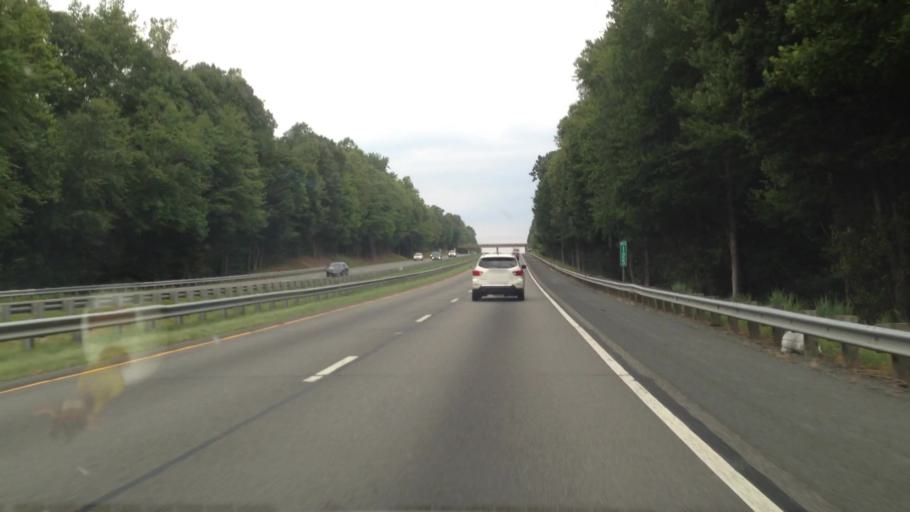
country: US
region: North Carolina
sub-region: Stokes County
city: King
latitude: 36.2800
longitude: -80.3869
